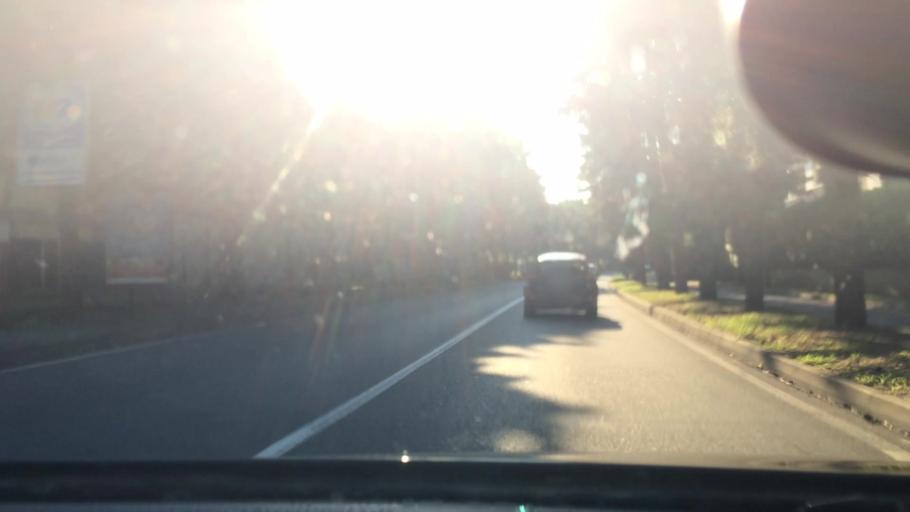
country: IT
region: Lombardy
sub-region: Citta metropolitana di Milano
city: Passirana
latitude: 45.5341
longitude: 9.0278
